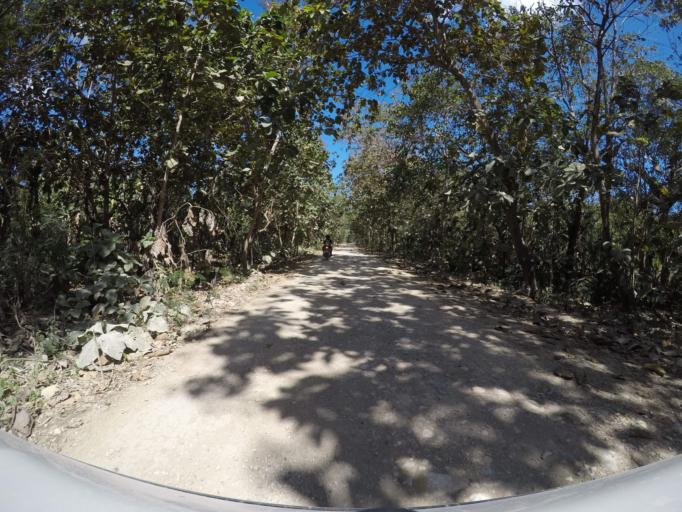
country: TL
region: Viqueque
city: Viqueque
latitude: -8.9316
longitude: 126.4109
